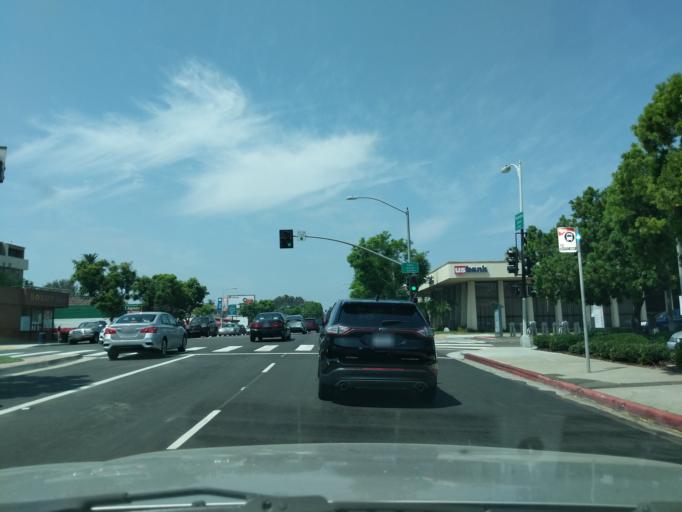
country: US
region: California
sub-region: San Diego County
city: San Diego
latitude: 32.7499
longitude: -117.1684
